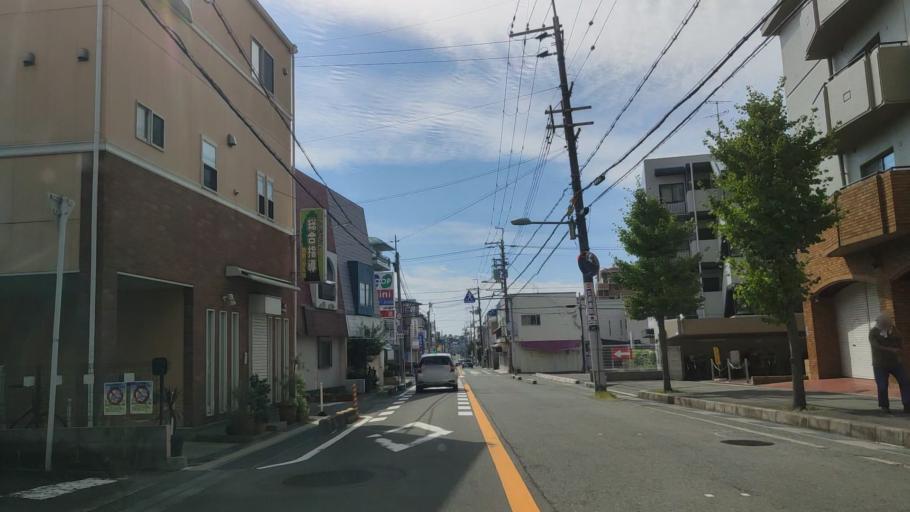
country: JP
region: Osaka
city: Toyonaka
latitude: 34.7986
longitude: 135.4638
